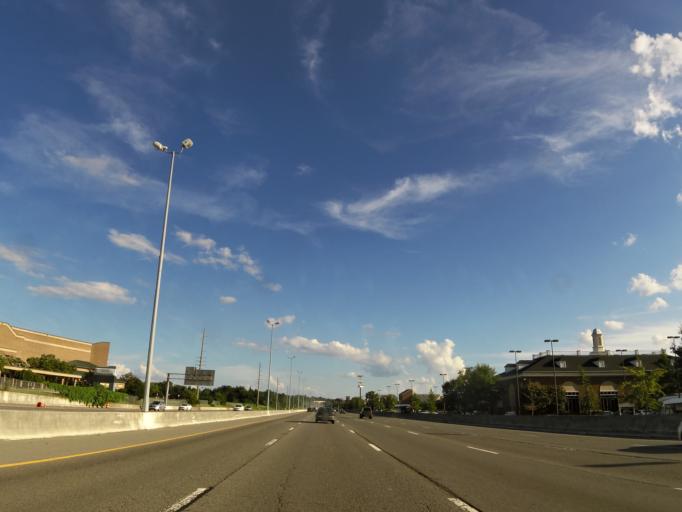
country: US
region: Tennessee
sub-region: Davidson County
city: Lakewood
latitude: 36.2138
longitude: -86.6920
